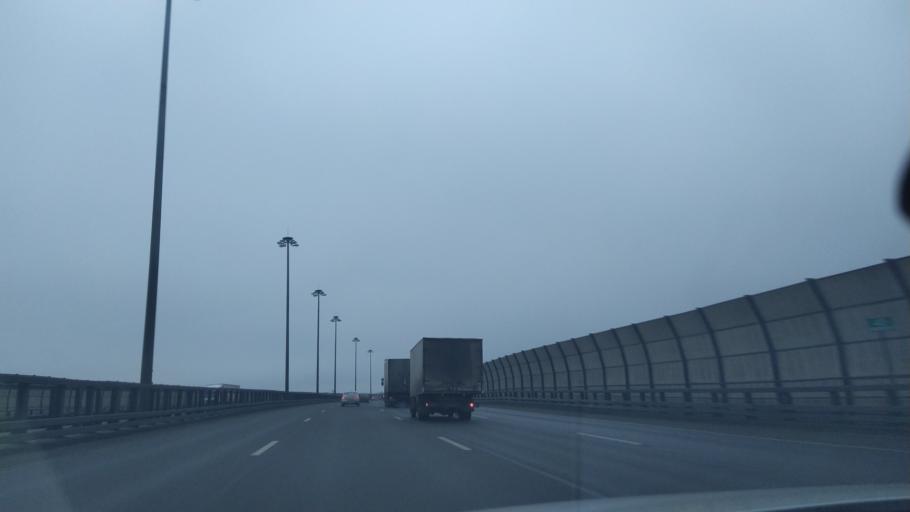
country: RU
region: St.-Petersburg
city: Krasnogvargeisky
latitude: 59.9811
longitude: 30.5175
